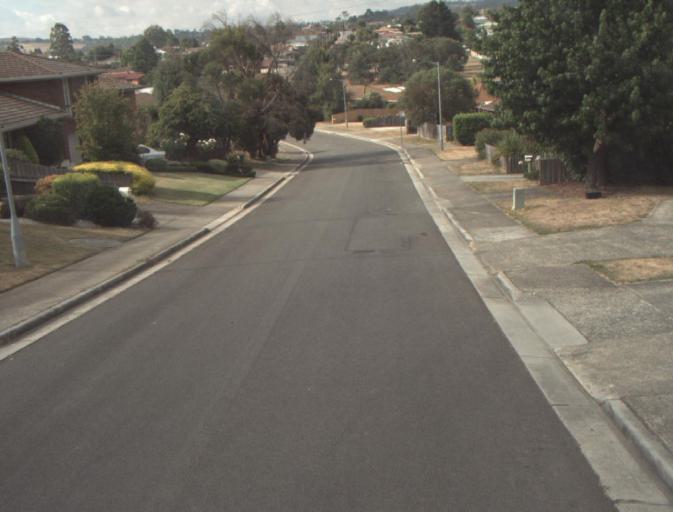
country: AU
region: Tasmania
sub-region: Launceston
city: Summerhill
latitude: -41.4824
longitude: 147.1716
